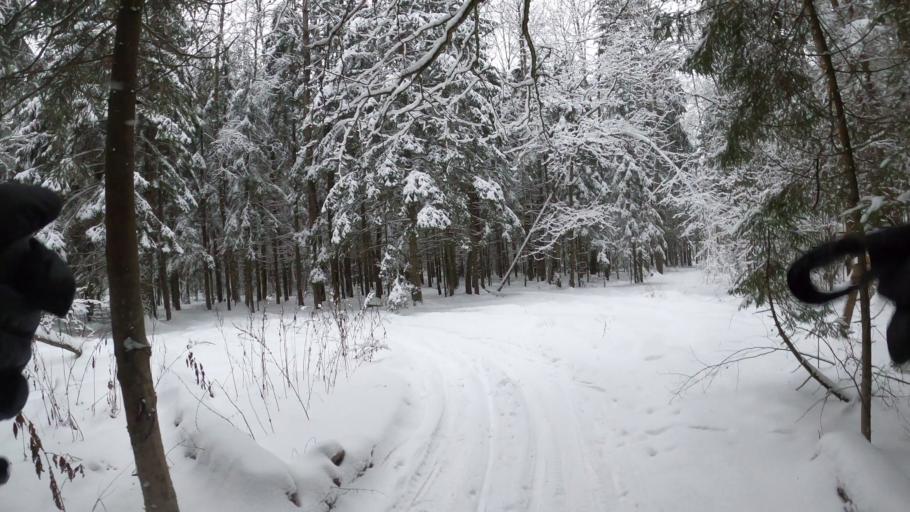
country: RU
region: Moskovskaya
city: Firsanovka
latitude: 55.9240
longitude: 37.2139
